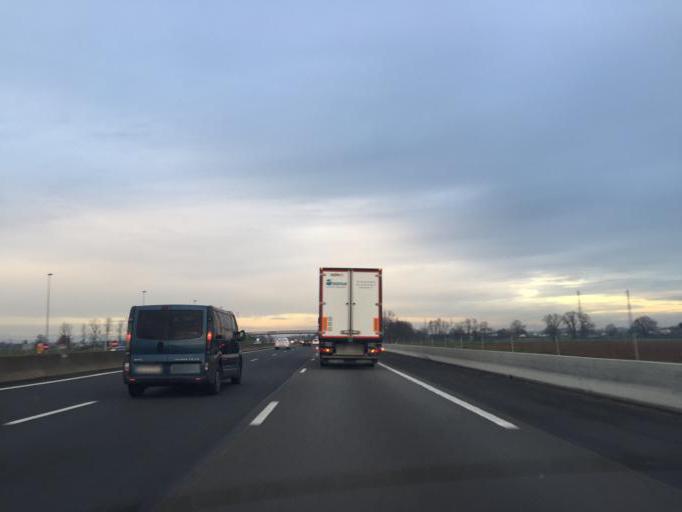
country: FR
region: Rhone-Alpes
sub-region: Departement de l'Ain
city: Guereins
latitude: 46.1448
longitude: 4.7692
